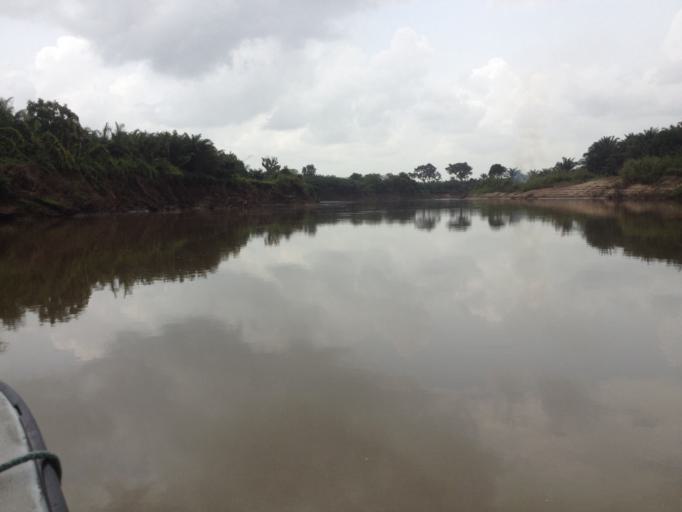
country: BJ
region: Mono
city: Lokossa
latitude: 6.5036
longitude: 1.6989
